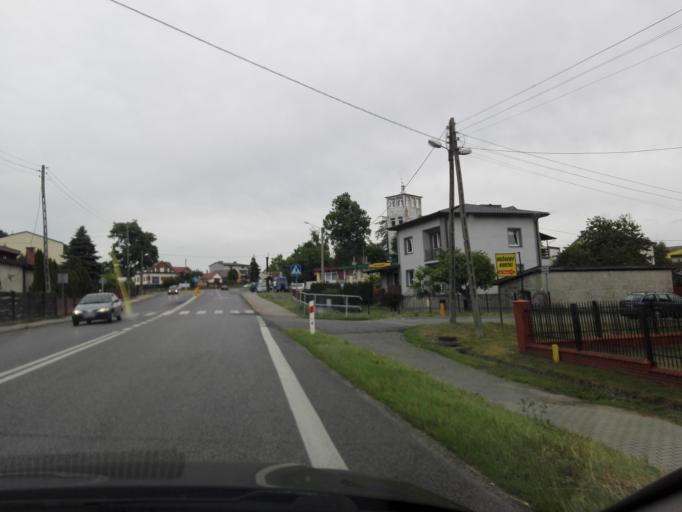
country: PL
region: Lublin Voivodeship
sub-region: Powiat pulawski
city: Kurow
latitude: 51.3889
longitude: 22.1828
